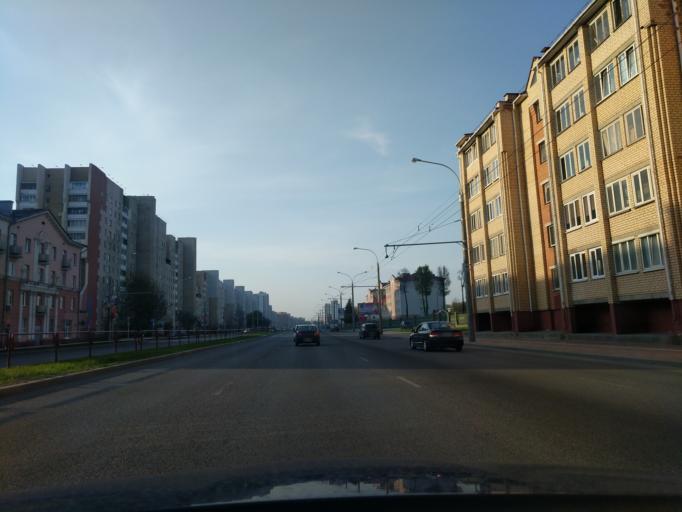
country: BY
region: Minsk
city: Minsk
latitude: 53.8654
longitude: 27.5710
